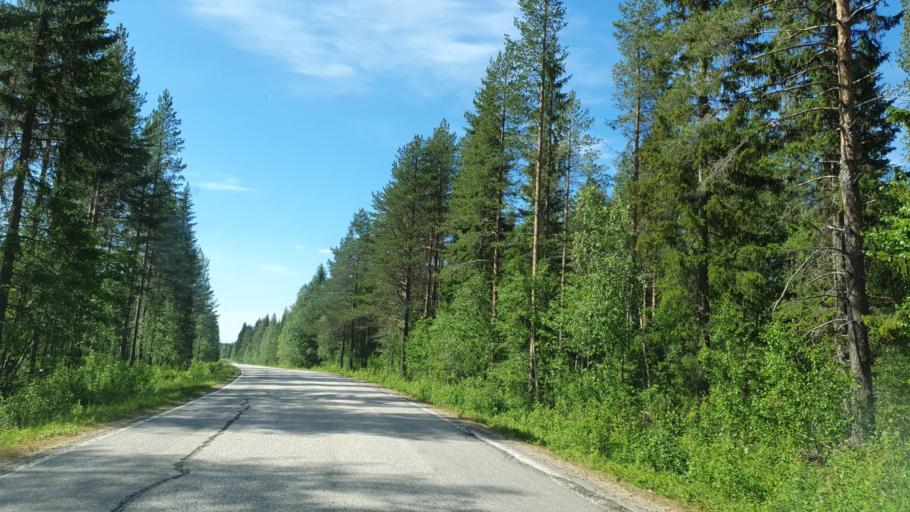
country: FI
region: Kainuu
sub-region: Kehys-Kainuu
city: Suomussalmi
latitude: 64.5792
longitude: 29.0381
